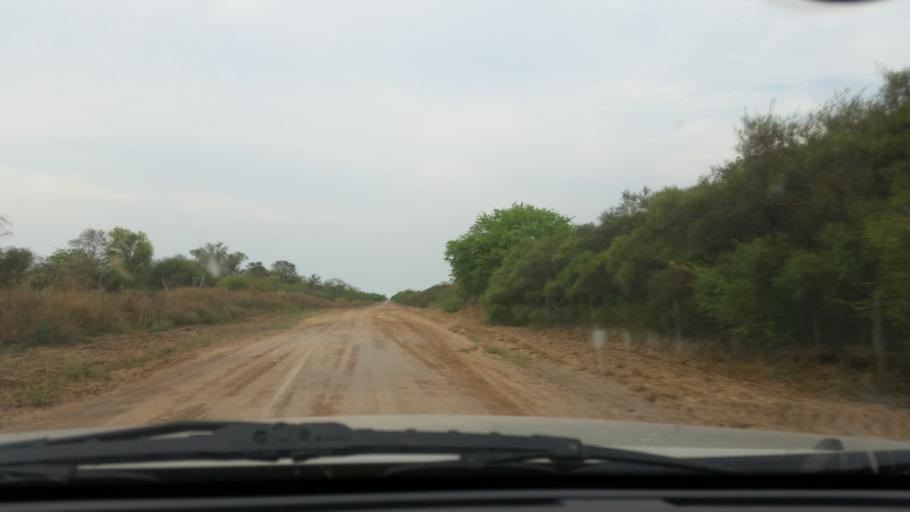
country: PY
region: Boqueron
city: Colonia Menno
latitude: -22.4729
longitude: -59.3395
